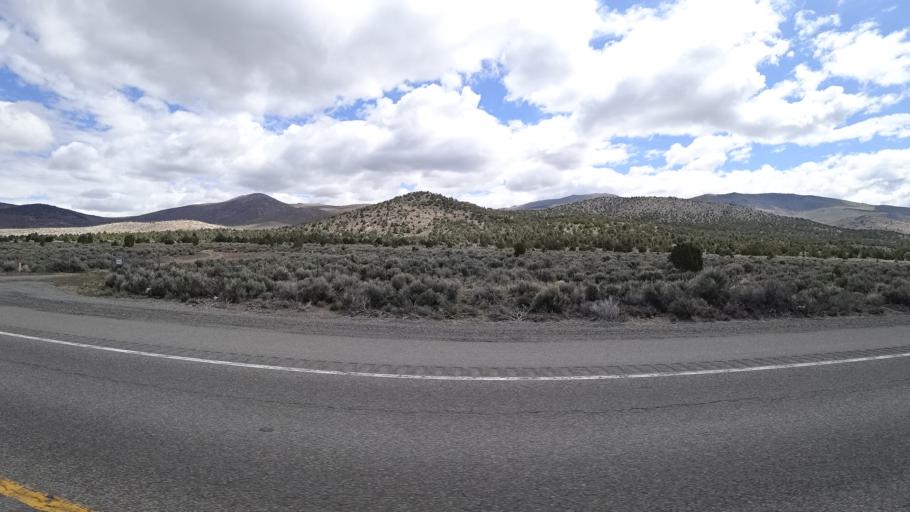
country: US
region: Nevada
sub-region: Douglas County
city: Gardnerville Ranchos
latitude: 38.8012
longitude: -119.6051
